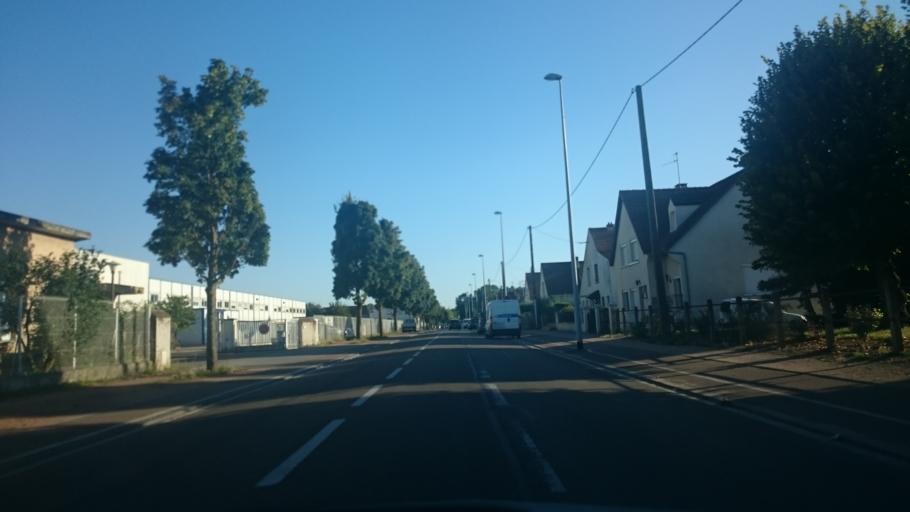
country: FR
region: Bourgogne
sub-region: Departement de la Cote-d'Or
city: Saint-Apollinaire
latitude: 47.3404
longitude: 5.0575
